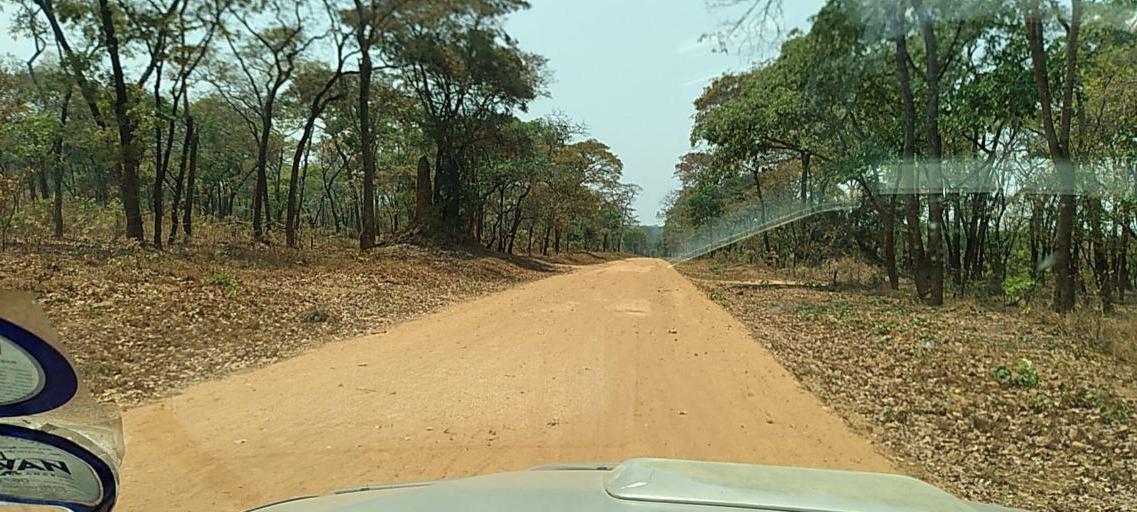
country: ZM
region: North-Western
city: Kasempa
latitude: -13.5469
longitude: 26.0360
